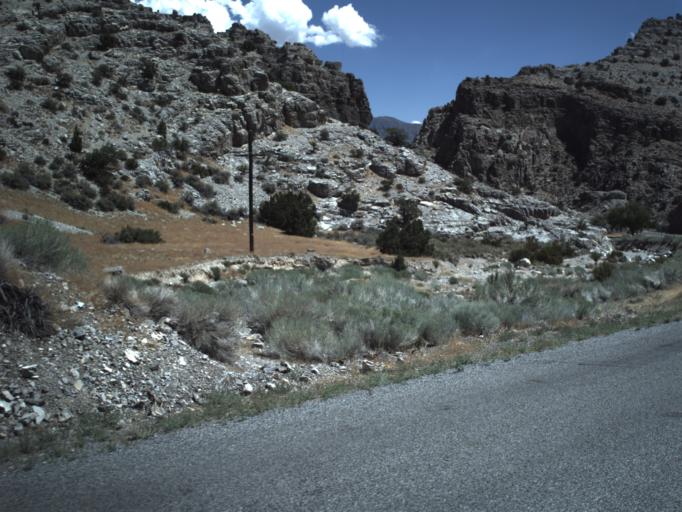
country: US
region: Utah
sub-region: Beaver County
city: Milford
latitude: 39.0843
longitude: -113.5751
